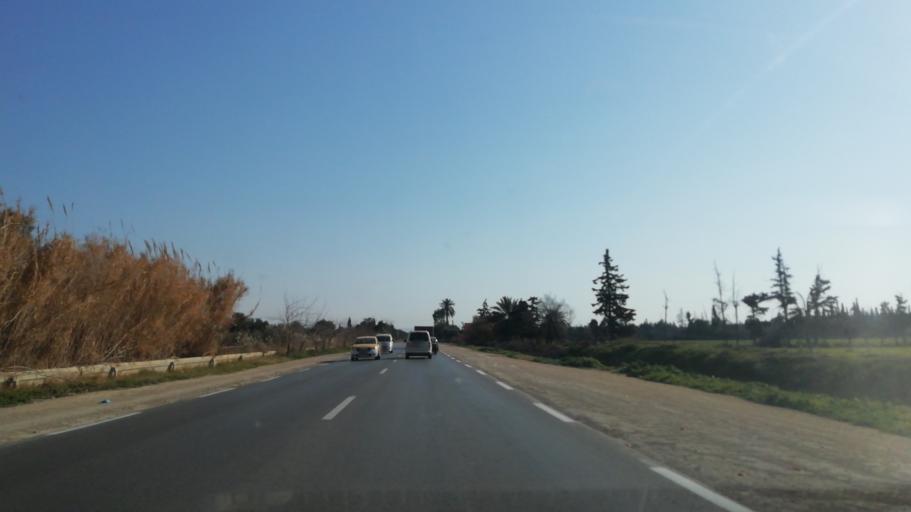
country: DZ
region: Relizane
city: Relizane
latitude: 35.7226
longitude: 0.4962
